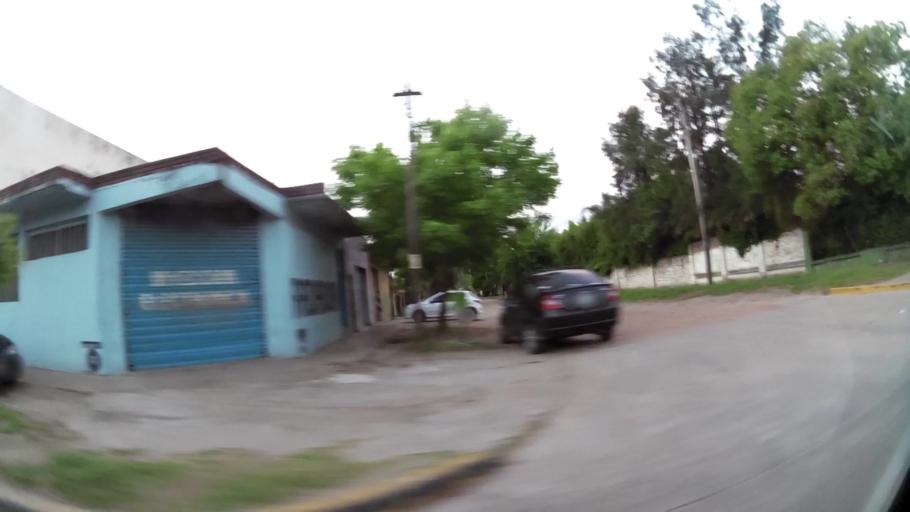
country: AR
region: Buenos Aires
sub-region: Partido de Merlo
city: Merlo
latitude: -34.6664
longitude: -58.7385
